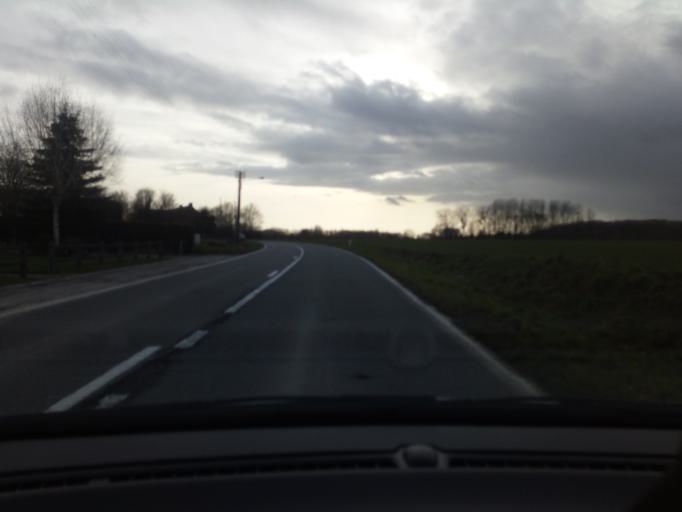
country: FR
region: Nord-Pas-de-Calais
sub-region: Departement du Nord
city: Feignies
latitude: 50.3456
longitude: 3.8792
